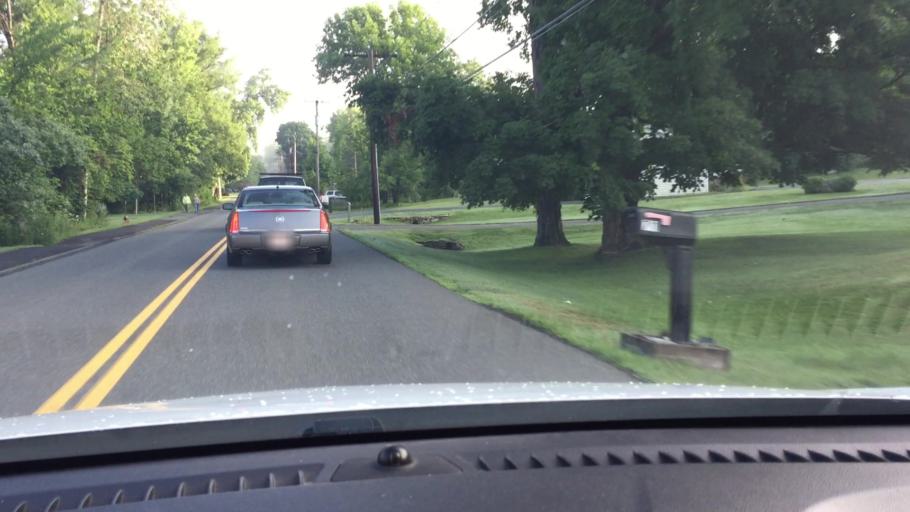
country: US
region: Massachusetts
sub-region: Berkshire County
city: Lee
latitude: 42.3207
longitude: -73.2371
